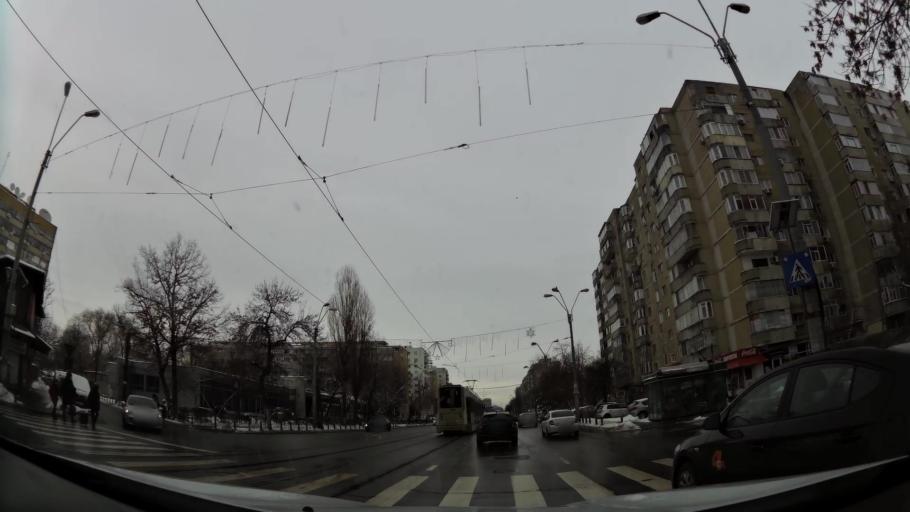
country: RO
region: Bucuresti
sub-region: Municipiul Bucuresti
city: Bucuresti
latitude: 44.3969
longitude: 26.1131
